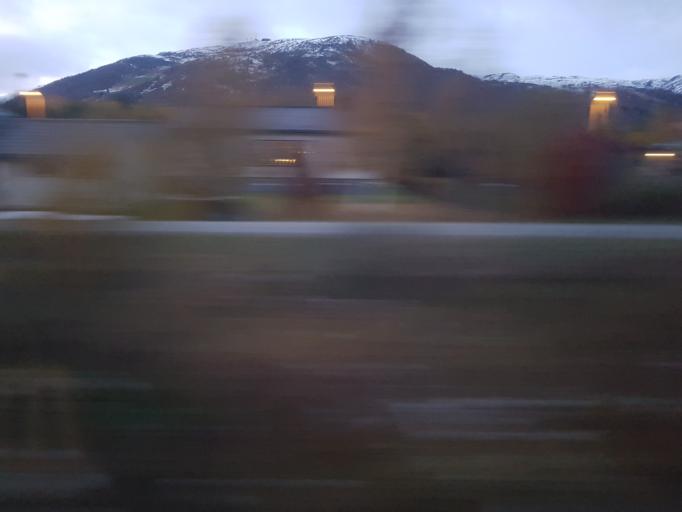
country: NO
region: Sor-Trondelag
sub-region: Oppdal
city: Oppdal
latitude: 62.5986
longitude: 9.7134
